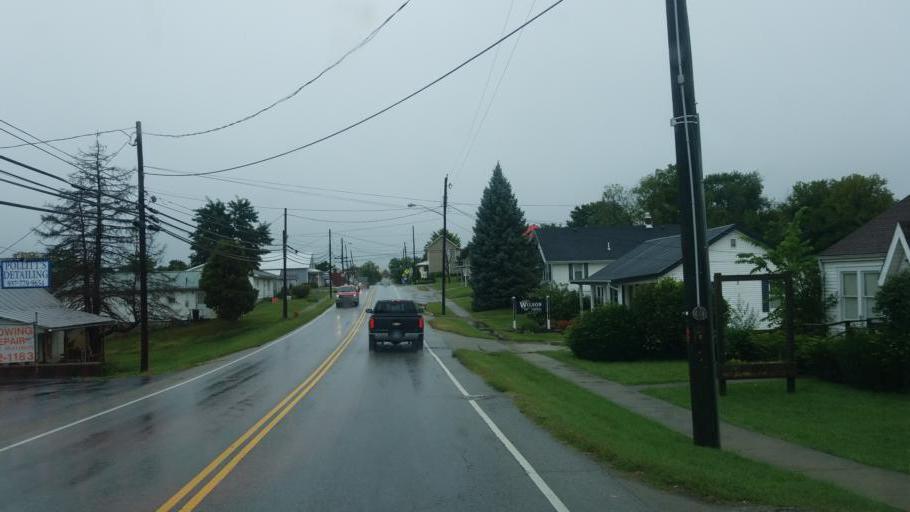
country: US
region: Ohio
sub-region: Adams County
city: West Union
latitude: 38.7945
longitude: -83.5416
